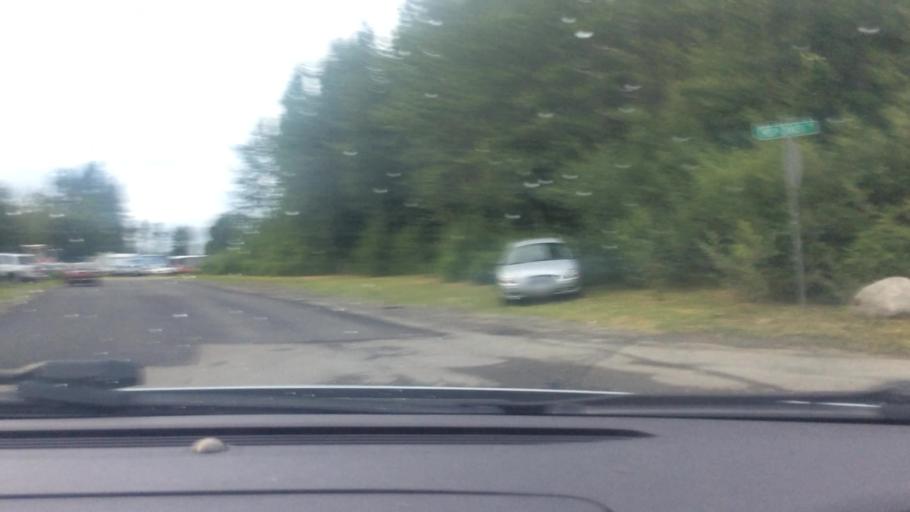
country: US
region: Alaska
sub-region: Anchorage Municipality
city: Elmendorf Air Force Base
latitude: 61.1983
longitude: -149.7258
